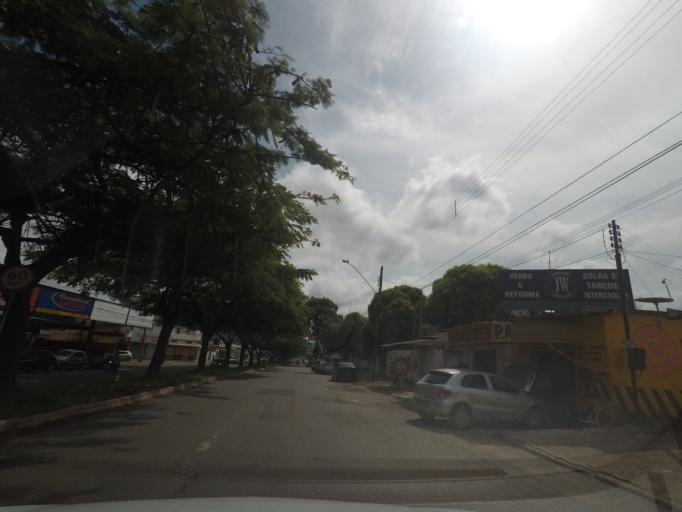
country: BR
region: Goias
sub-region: Goiania
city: Goiania
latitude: -16.6669
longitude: -49.2175
